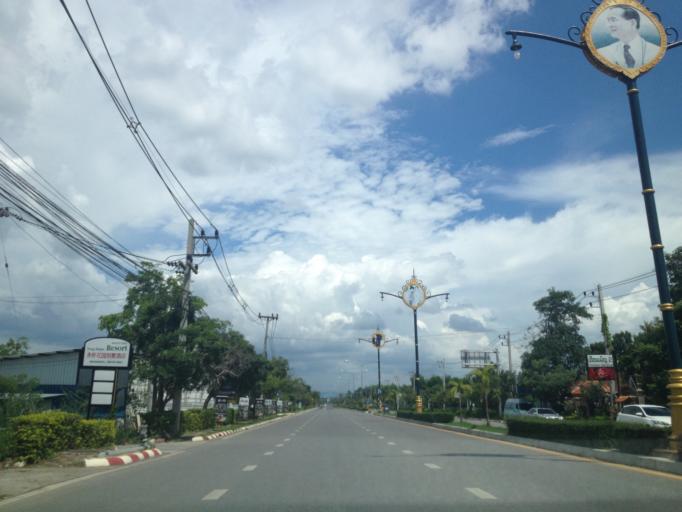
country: TH
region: Chiang Mai
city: Hang Dong
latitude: 18.7384
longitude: 98.9336
